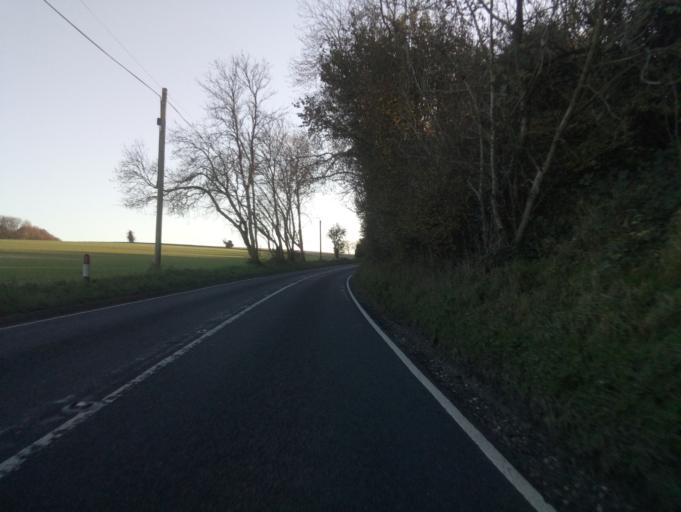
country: GB
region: England
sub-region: Wiltshire
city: Chicklade
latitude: 51.1255
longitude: -2.1633
